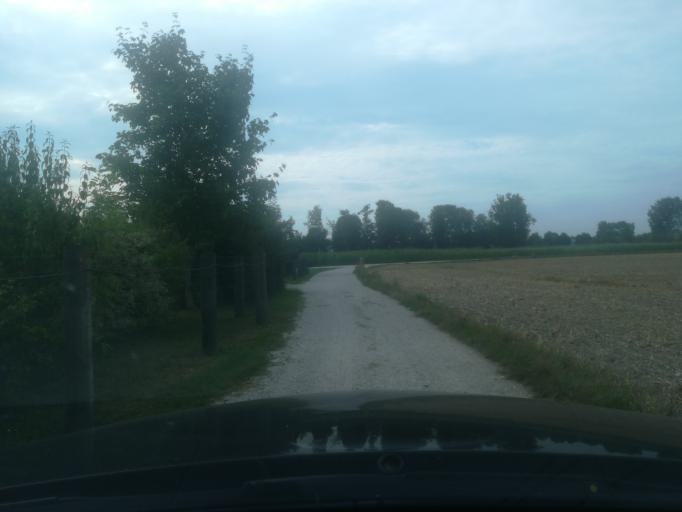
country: AT
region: Upper Austria
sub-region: Wels-Land
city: Marchtrenk
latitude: 48.1830
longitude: 14.1318
